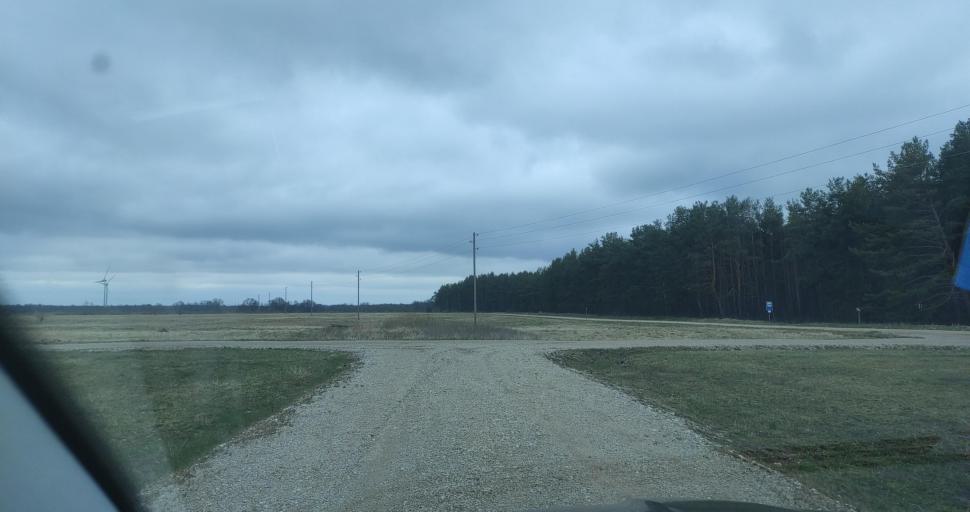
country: LV
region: Liepaja
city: Vec-Liepaja
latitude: 56.6402
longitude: 21.0458
